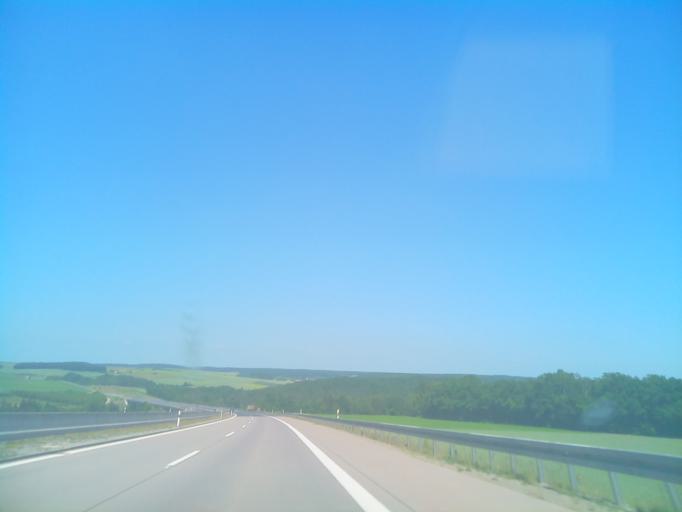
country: DE
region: Bavaria
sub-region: Regierungsbezirk Unterfranken
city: Hollstadt
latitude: 50.3380
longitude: 10.3034
